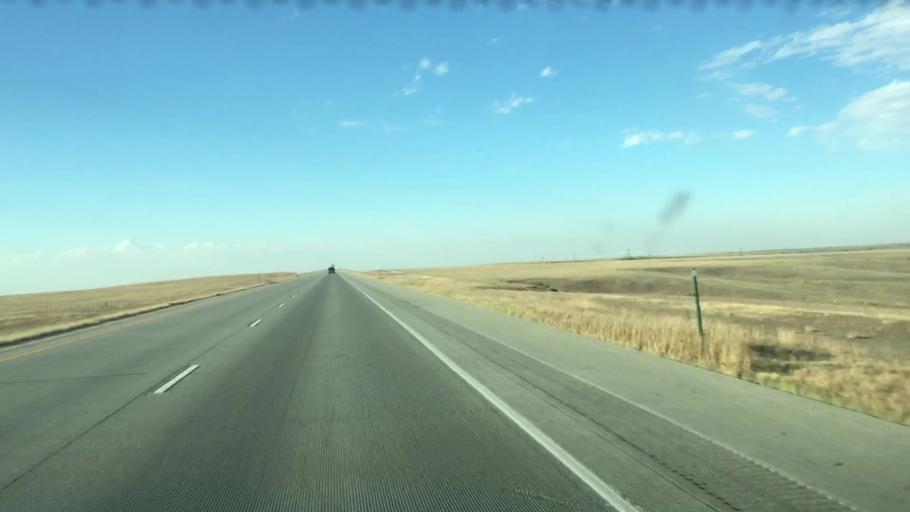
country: US
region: Colorado
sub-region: Lincoln County
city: Limon
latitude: 39.3839
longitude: -103.8872
